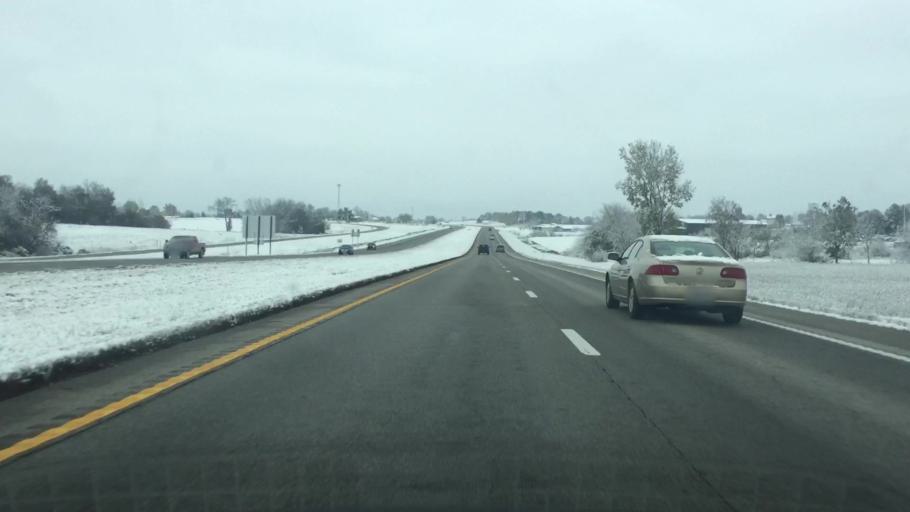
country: US
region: Missouri
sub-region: Cass County
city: Garden City
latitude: 38.5614
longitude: -94.1831
